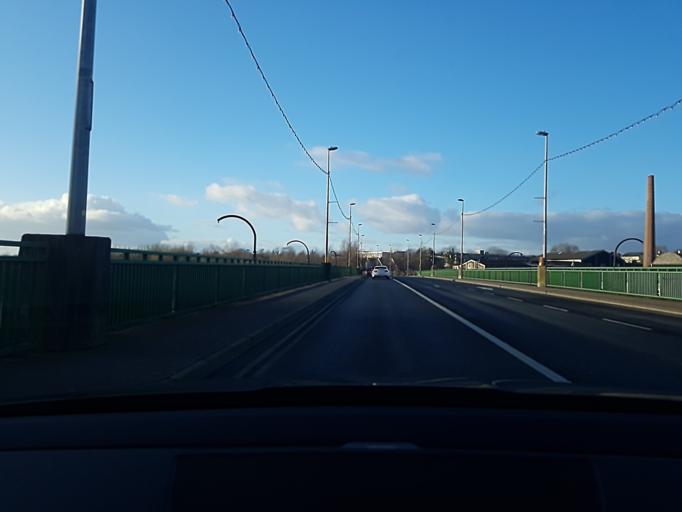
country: IE
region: Munster
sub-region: County Limerick
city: Luimneach
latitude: 52.6620
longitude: -8.6347
